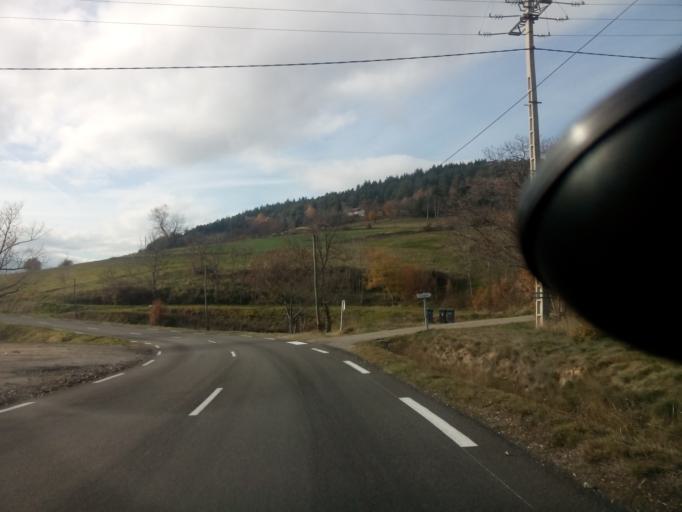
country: FR
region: Rhone-Alpes
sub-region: Departement de la Loire
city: Saint-Julien-Molin-Molette
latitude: 45.3311
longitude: 4.6389
